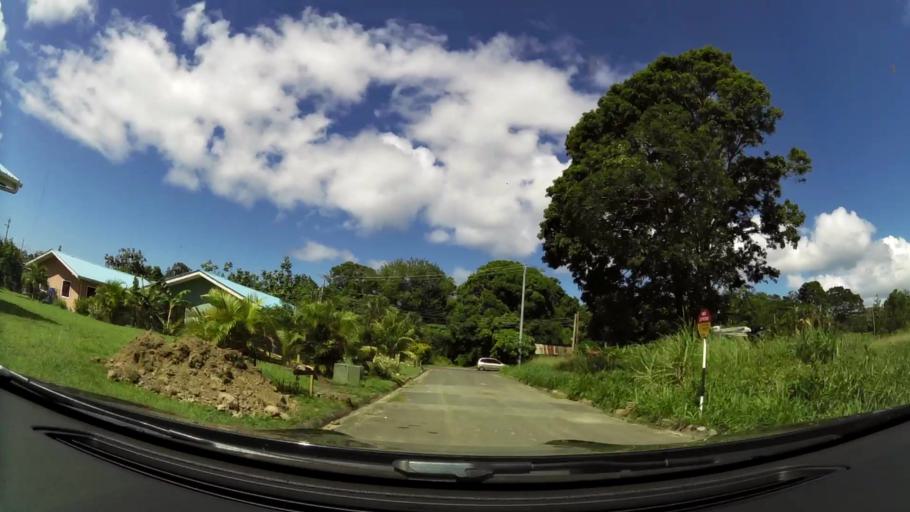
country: TT
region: Tobago
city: Scarborough
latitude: 11.2212
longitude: -60.7678
